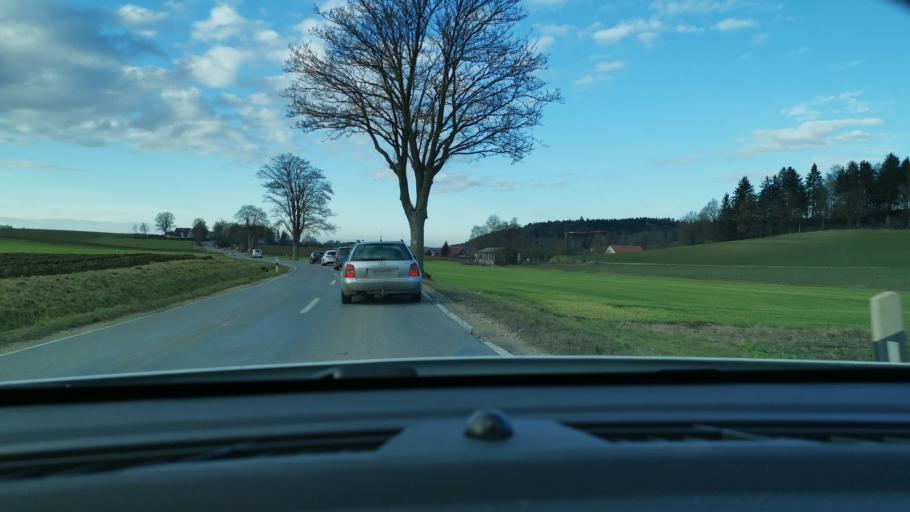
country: DE
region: Bavaria
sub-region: Swabia
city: Petersdorf
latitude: 48.5521
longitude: 10.9950
